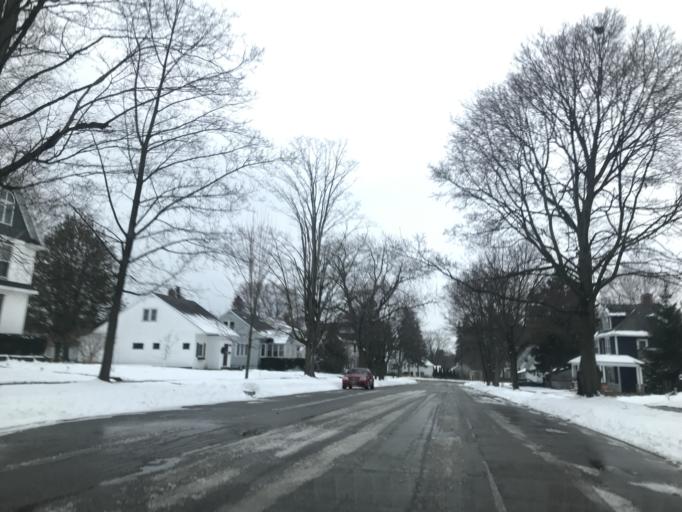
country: US
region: Wisconsin
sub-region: Door County
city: Sturgeon Bay
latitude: 44.8365
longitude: -87.3710
